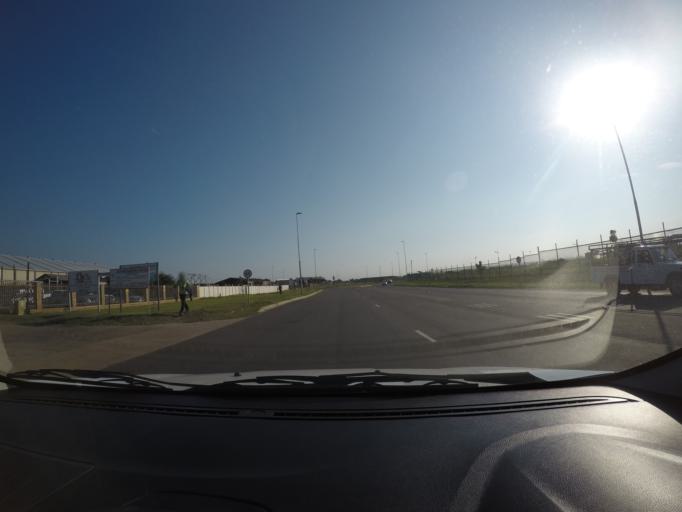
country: ZA
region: KwaZulu-Natal
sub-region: uThungulu District Municipality
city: Richards Bay
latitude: -28.7436
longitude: 32.0353
